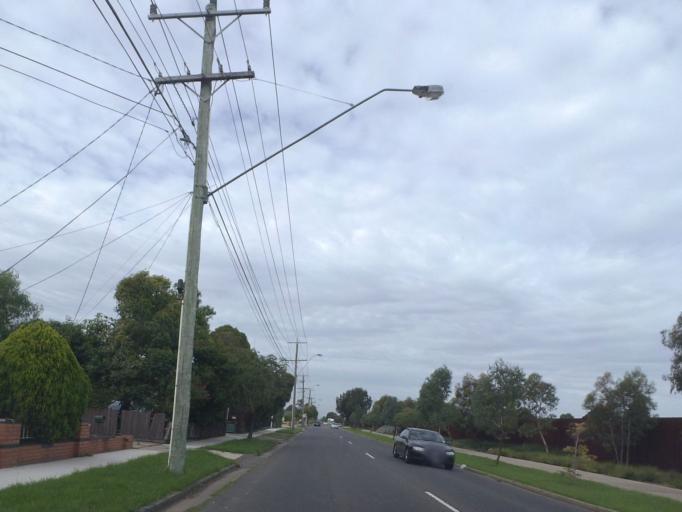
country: AU
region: Victoria
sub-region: Brimbank
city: Sunshine West
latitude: -37.7823
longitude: 144.7978
